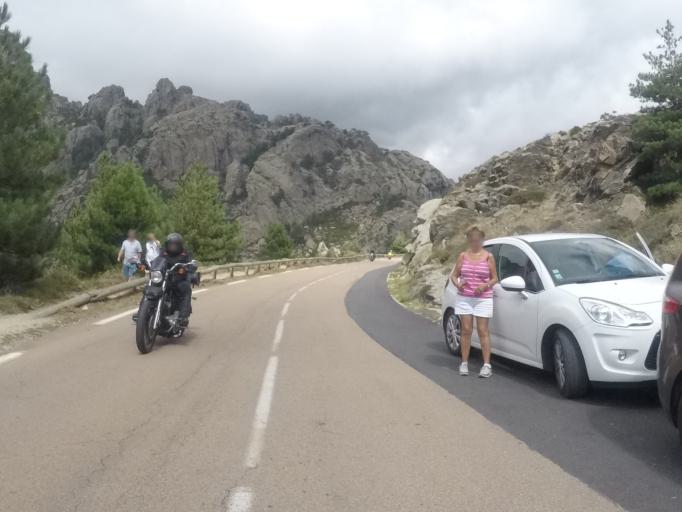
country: FR
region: Corsica
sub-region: Departement de la Corse-du-Sud
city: Zonza
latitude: 41.7937
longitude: 9.2225
